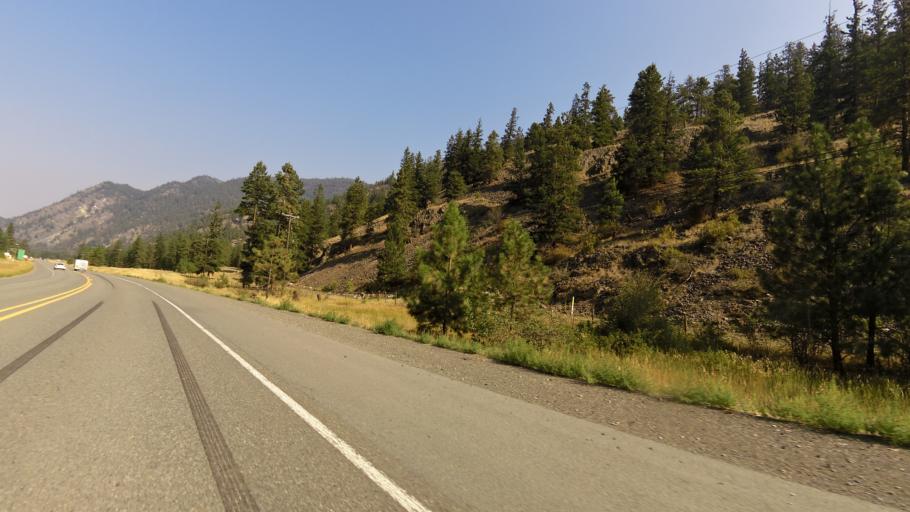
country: CA
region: British Columbia
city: Princeton
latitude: 49.3718
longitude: -120.1364
